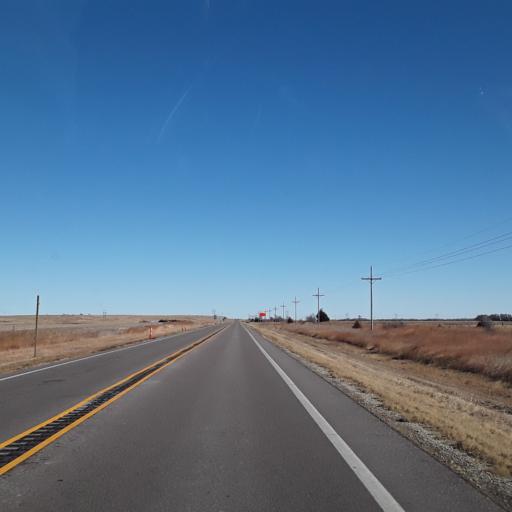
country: US
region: Kansas
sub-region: Pawnee County
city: Larned
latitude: 38.0808
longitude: -99.2356
